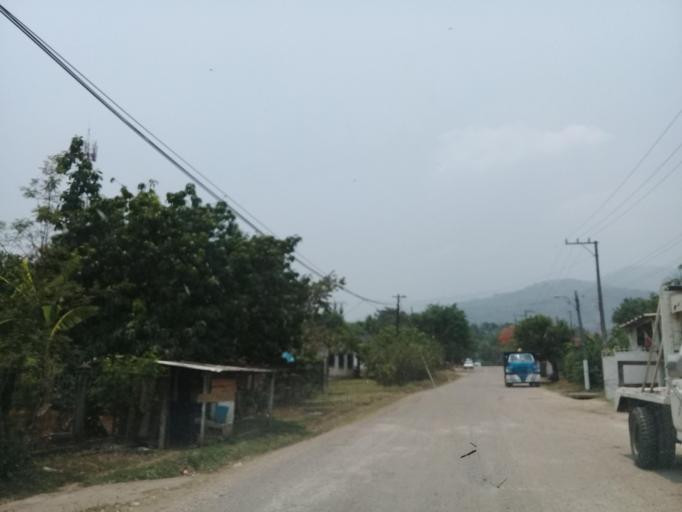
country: MX
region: Veracruz
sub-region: Tezonapa
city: Laguna Chica (Pueblo Nuevo)
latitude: 18.5421
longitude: -96.7344
